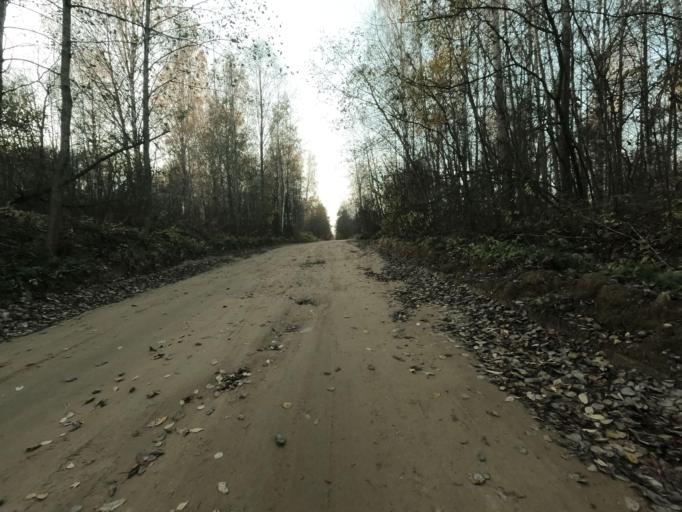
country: RU
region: Leningrad
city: Mga
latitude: 59.7598
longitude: 31.2639
